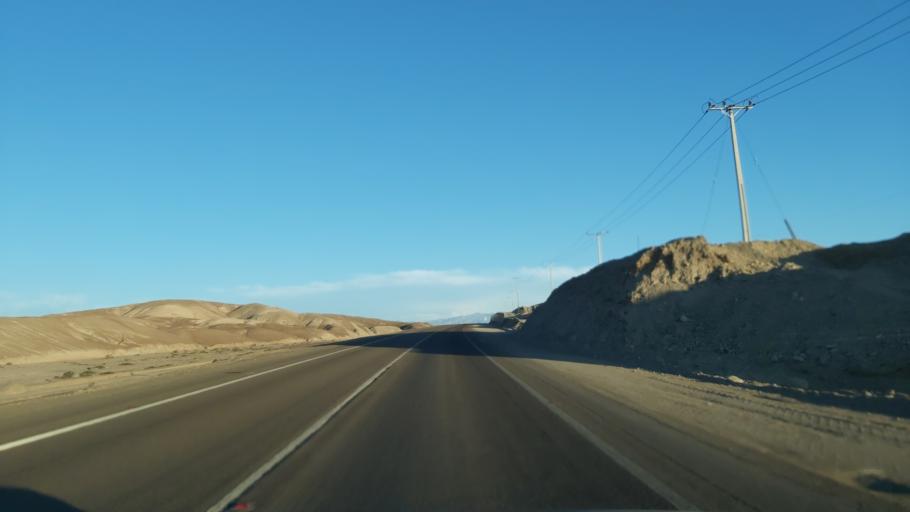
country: CL
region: Atacama
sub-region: Provincia de Chanaral
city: Diego de Almagro
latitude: -26.4184
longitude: -70.0273
